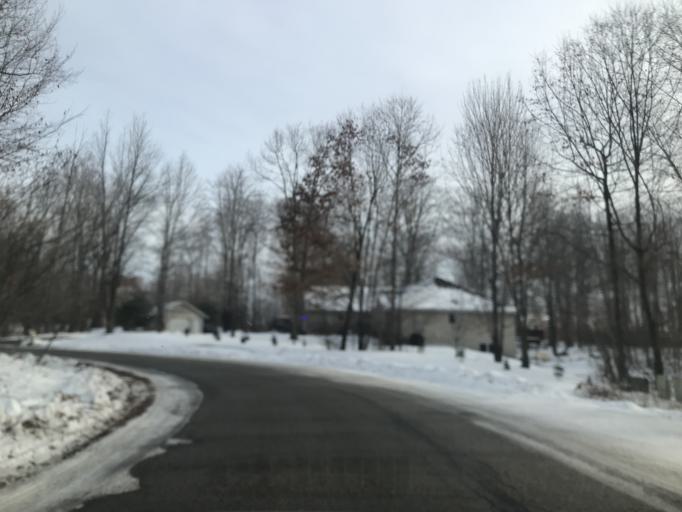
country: US
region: Wisconsin
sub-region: Brown County
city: Suamico
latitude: 44.6891
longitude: -88.0532
